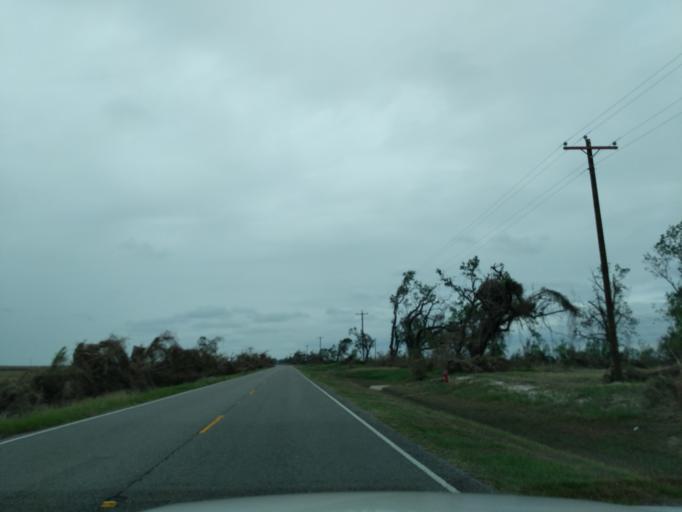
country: US
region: Louisiana
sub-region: Cameron Parish
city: Cameron
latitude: 29.7866
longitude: -93.1259
